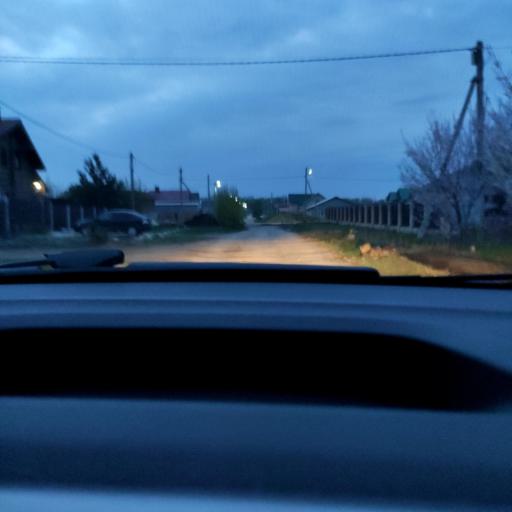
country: RU
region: Samara
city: Tol'yatti
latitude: 53.5506
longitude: 49.4048
